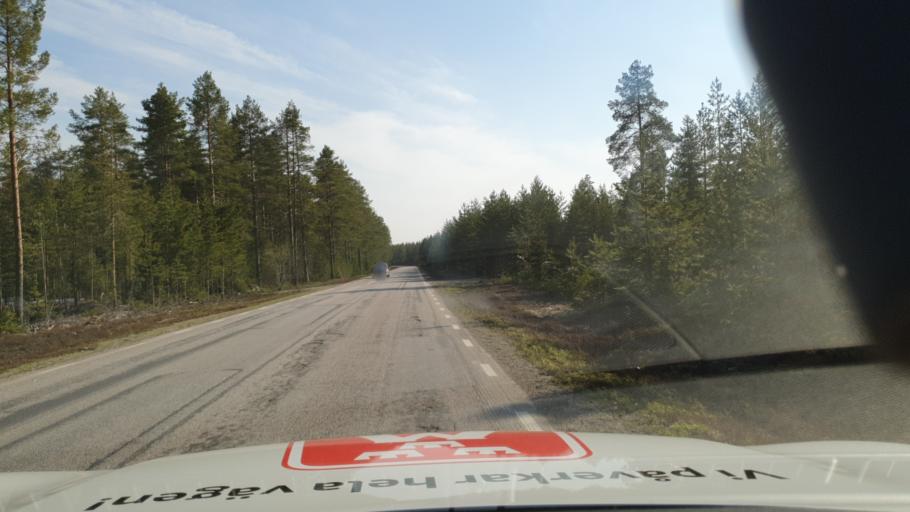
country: SE
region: Vaesterbotten
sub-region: Umea Kommun
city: Roback
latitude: 63.8708
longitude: 20.1487
